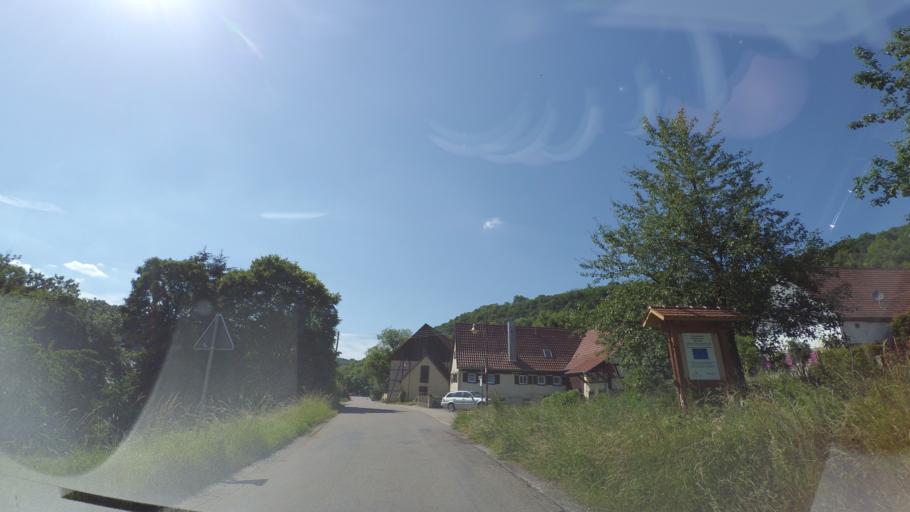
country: DE
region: Baden-Wuerttemberg
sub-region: Regierungsbezirk Stuttgart
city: Wolpertshausen
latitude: 49.1401
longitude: 9.8522
